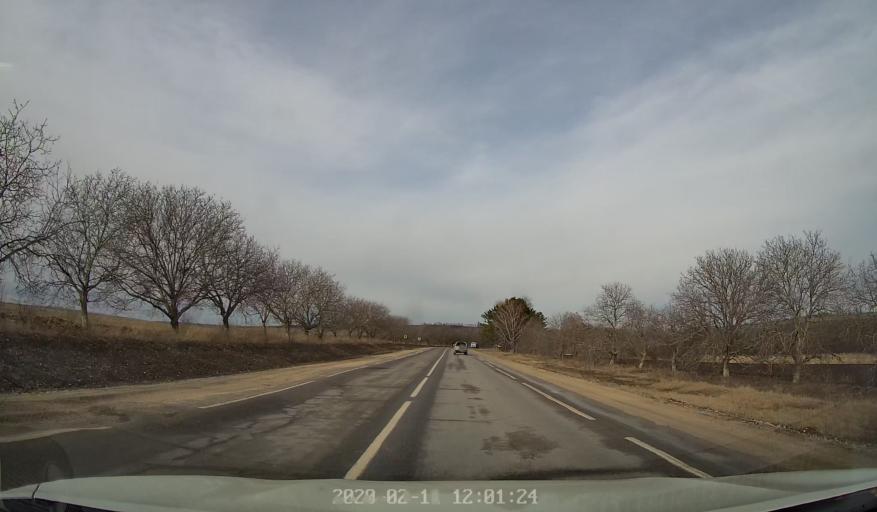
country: MD
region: Riscani
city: Riscani
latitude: 47.9385
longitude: 27.6291
